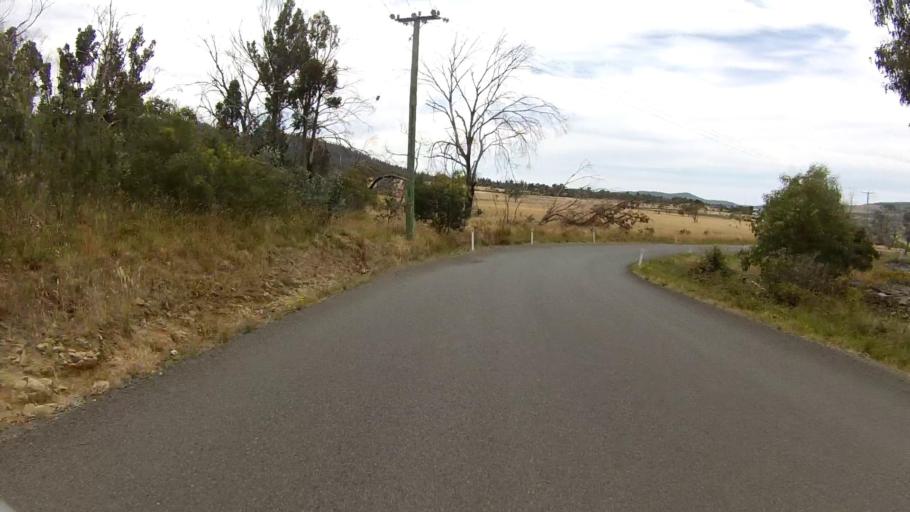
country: AU
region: Tasmania
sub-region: Sorell
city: Sorell
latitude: -42.8910
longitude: 147.7907
